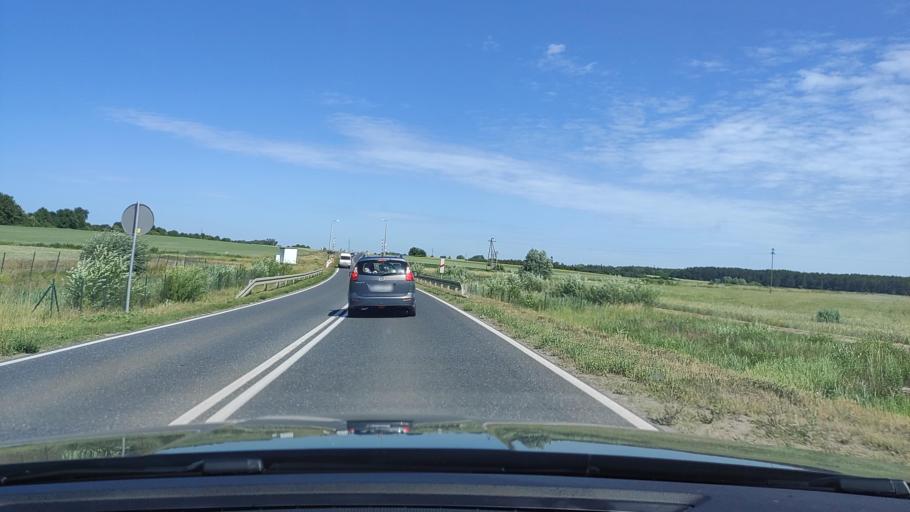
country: PL
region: Greater Poland Voivodeship
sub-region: Powiat poznanski
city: Murowana Goslina
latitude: 52.5515
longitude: 16.9914
